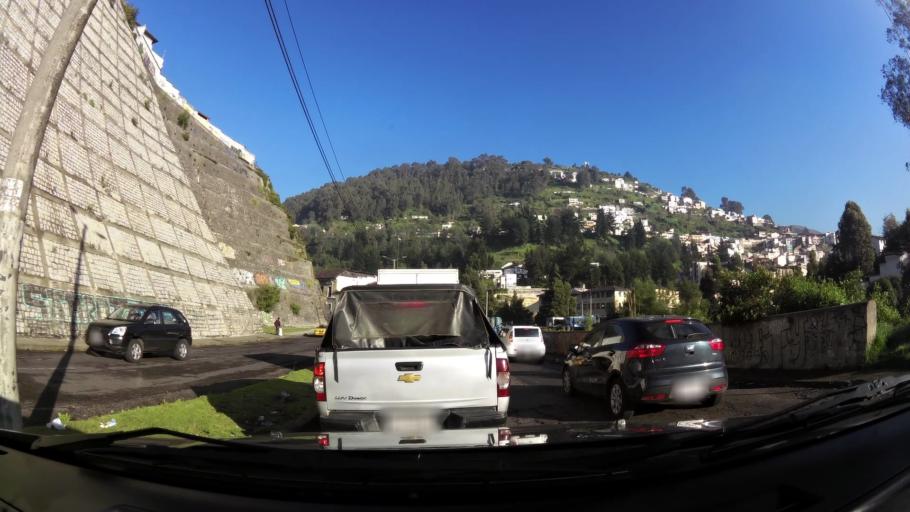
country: EC
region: Pichincha
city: Quito
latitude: -0.2338
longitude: -78.5132
